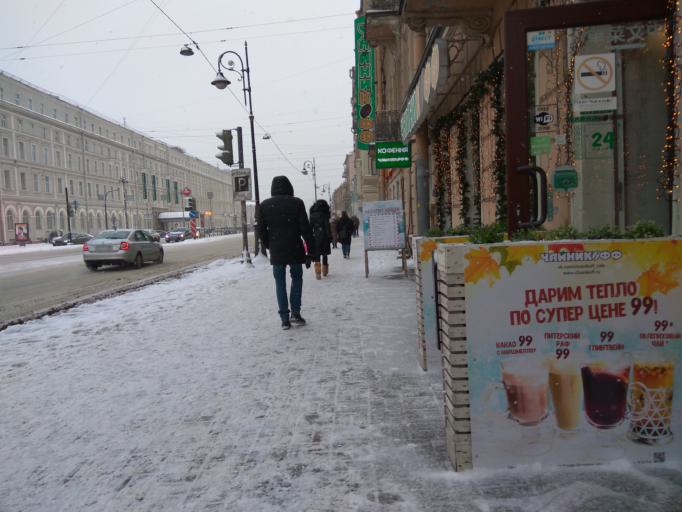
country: RU
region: St.-Petersburg
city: Centralniy
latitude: 59.9339
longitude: 30.3624
